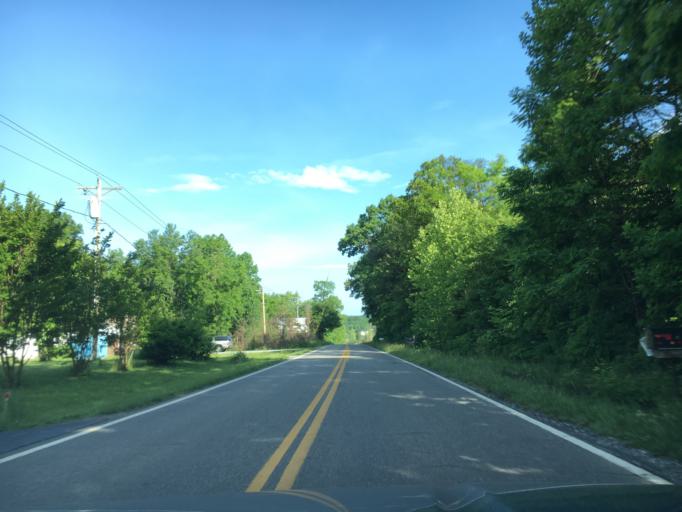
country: US
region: Virginia
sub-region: Campbell County
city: Rustburg
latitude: 37.3074
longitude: -79.1676
